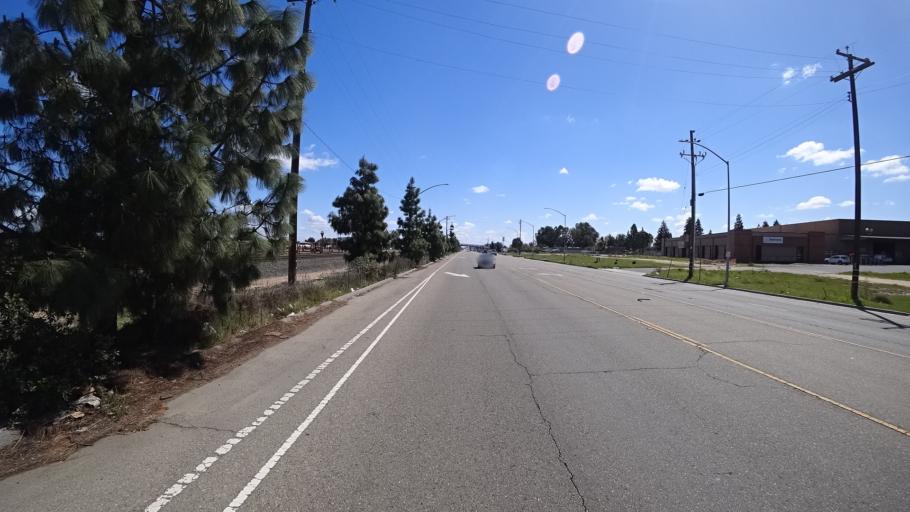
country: US
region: California
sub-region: Fresno County
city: West Park
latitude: 36.7987
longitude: -119.8670
